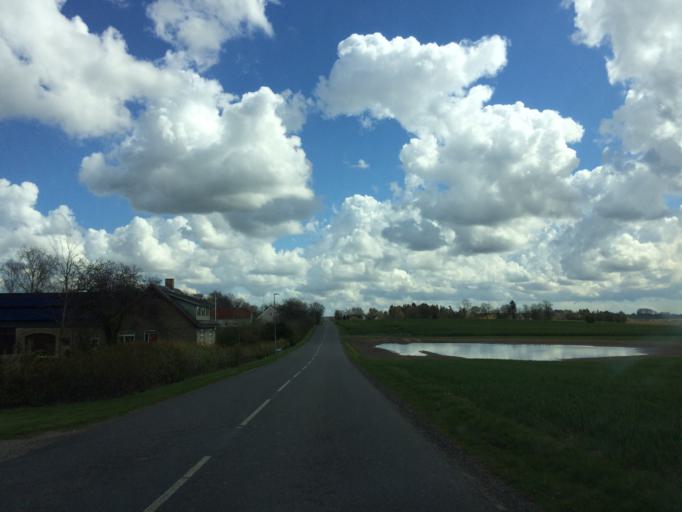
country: DK
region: South Denmark
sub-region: Assens Kommune
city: Tommerup
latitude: 55.2515
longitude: 10.2655
